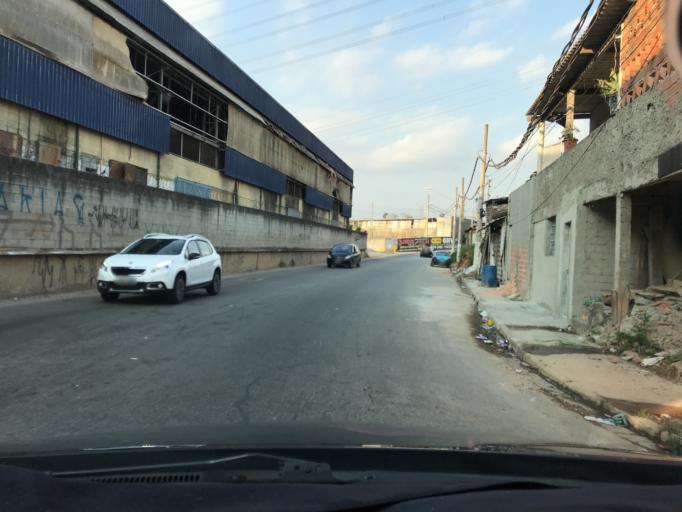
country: BR
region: Sao Paulo
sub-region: Osasco
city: Osasco
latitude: -23.5314
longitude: -46.7593
